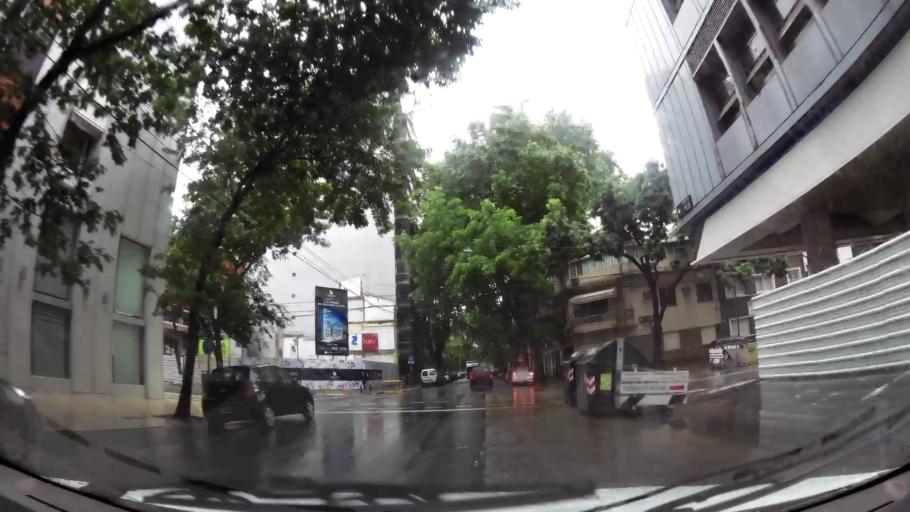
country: AR
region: Buenos Aires F.D.
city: Colegiales
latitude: -34.5738
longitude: -58.4214
